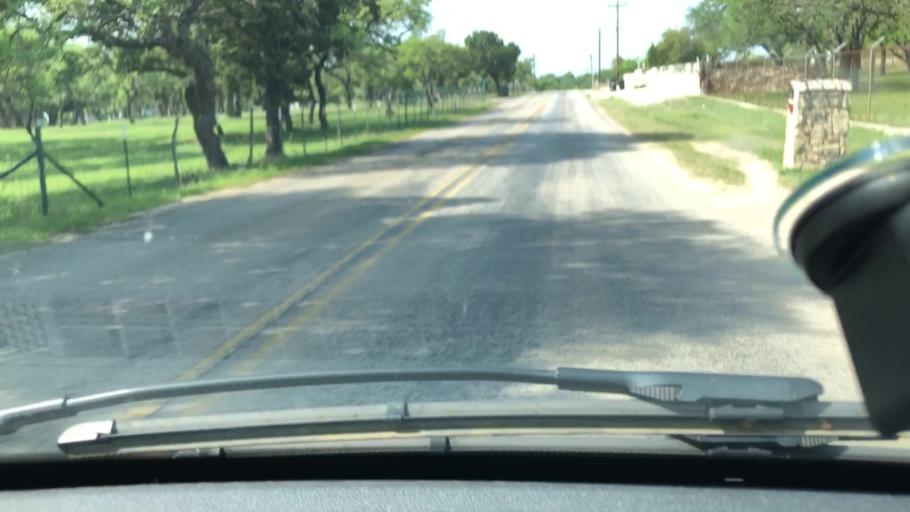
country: US
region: Texas
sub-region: Comal County
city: Bulverde
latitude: 29.7704
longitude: -98.4588
